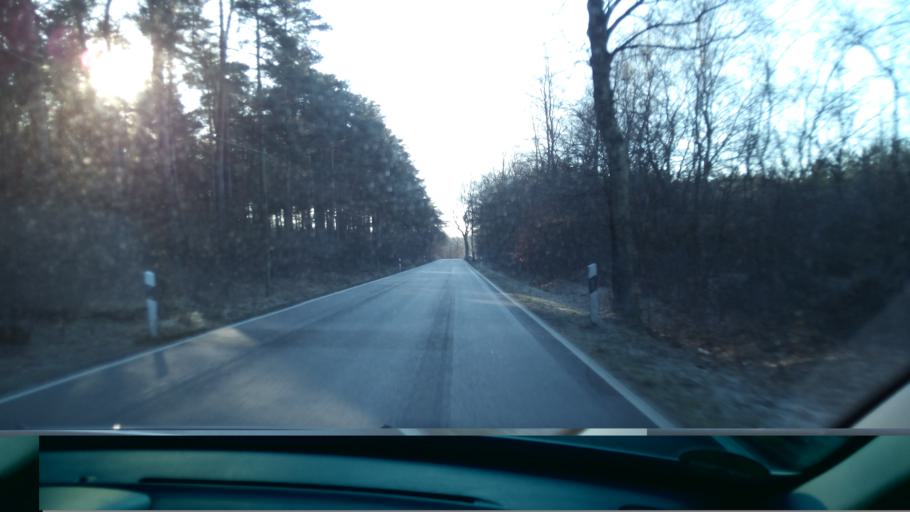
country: DE
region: Schleswig-Holstein
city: Brothen
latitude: 53.4989
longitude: 10.6789
